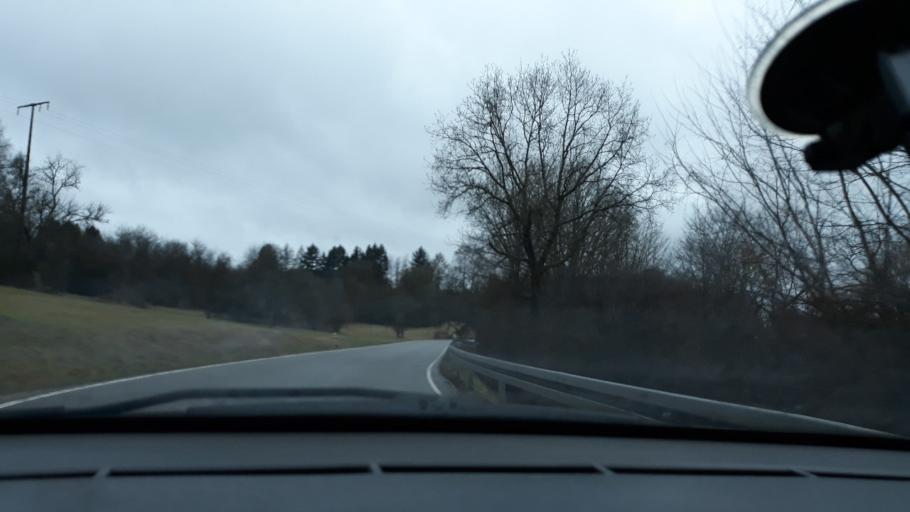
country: DE
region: Saarland
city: Blieskastel
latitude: 49.2315
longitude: 7.1933
